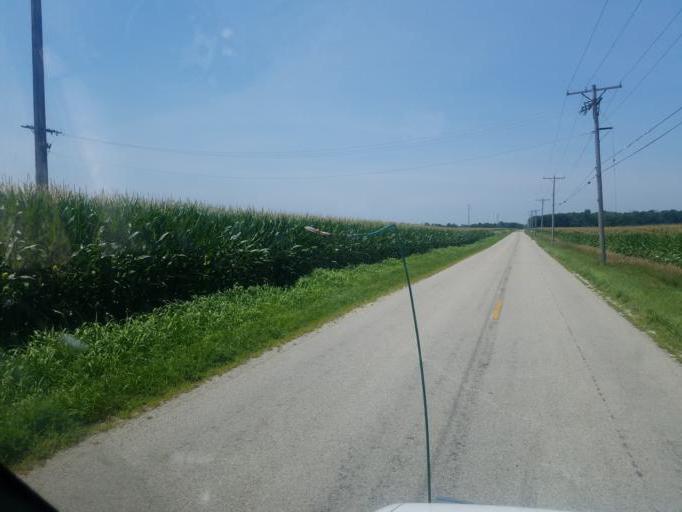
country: US
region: Ohio
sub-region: Shelby County
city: Sidney
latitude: 40.3046
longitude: -84.0849
